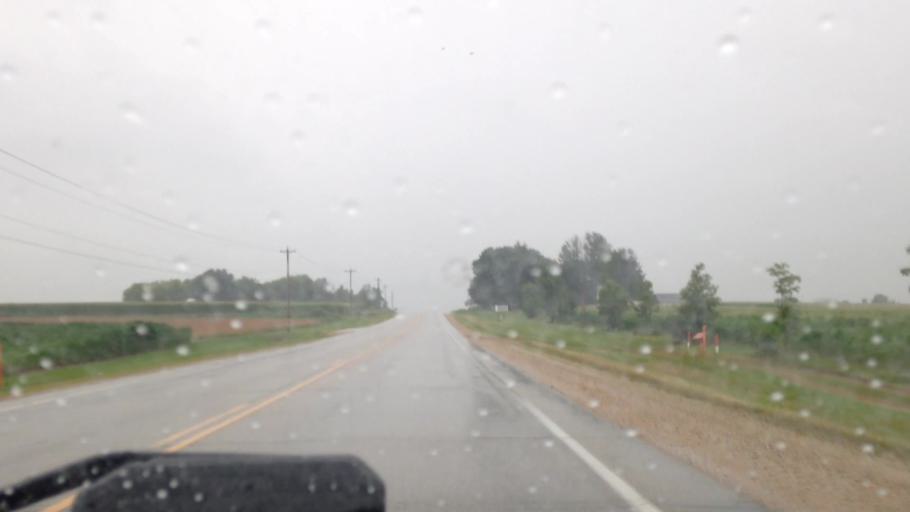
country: US
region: Wisconsin
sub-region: Washington County
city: Hartford
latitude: 43.4232
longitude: -88.3913
